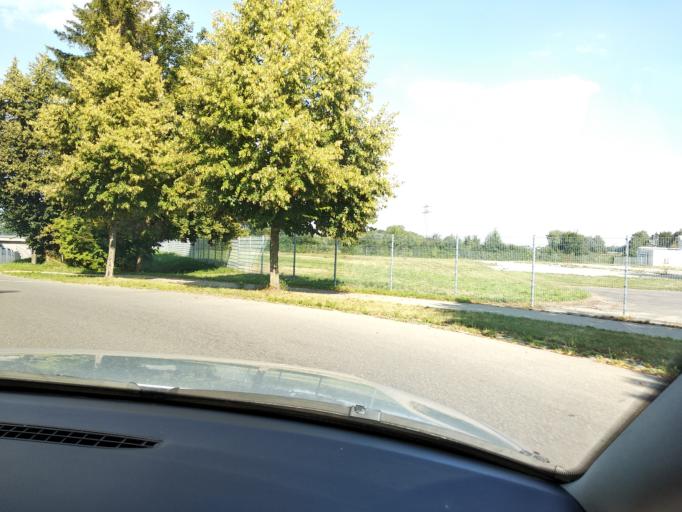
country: DE
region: Bavaria
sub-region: Swabia
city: Memmingen
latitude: 48.0035
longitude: 10.1853
